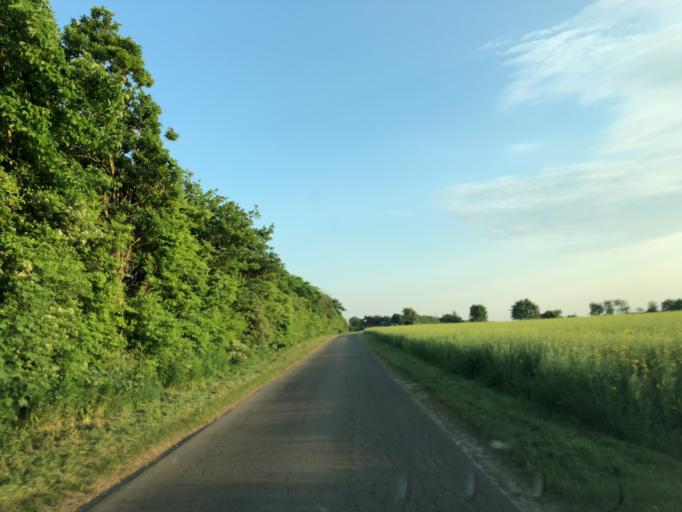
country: DK
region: Central Jutland
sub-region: Holstebro Kommune
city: Holstebro
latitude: 56.3961
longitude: 8.4833
